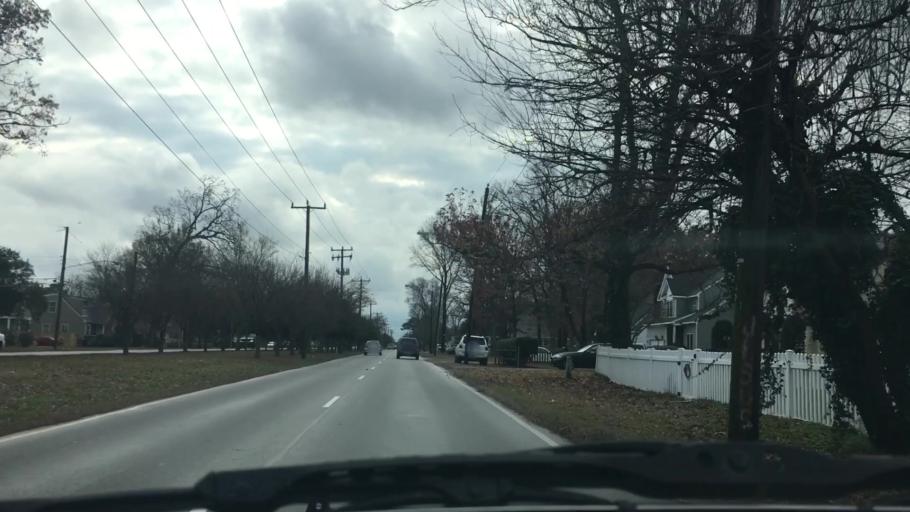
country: US
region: Virginia
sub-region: City of Norfolk
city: Norfolk
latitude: 36.9225
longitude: -76.2428
